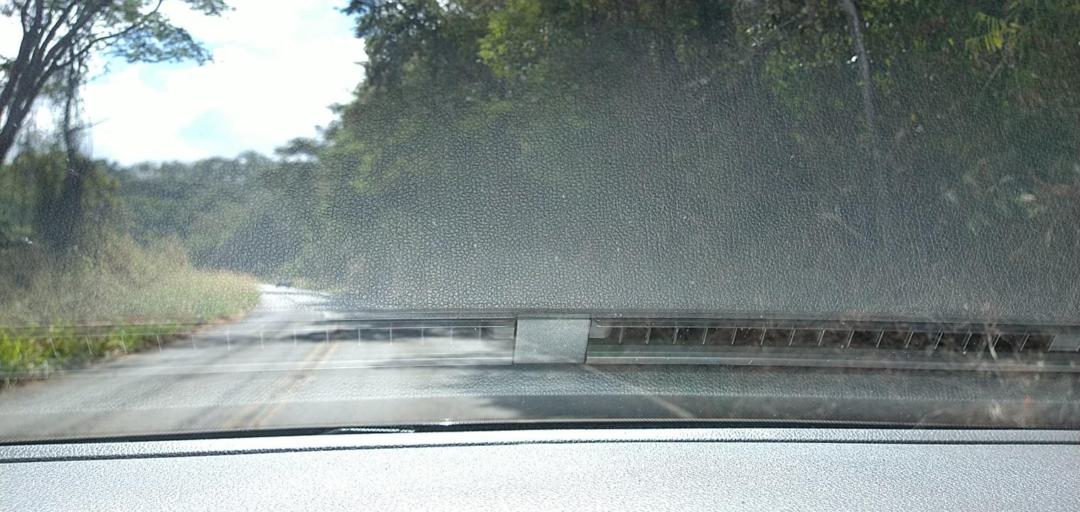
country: BR
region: Minas Gerais
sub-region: Ponte Nova
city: Ponte Nova
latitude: -20.2321
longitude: -42.9011
